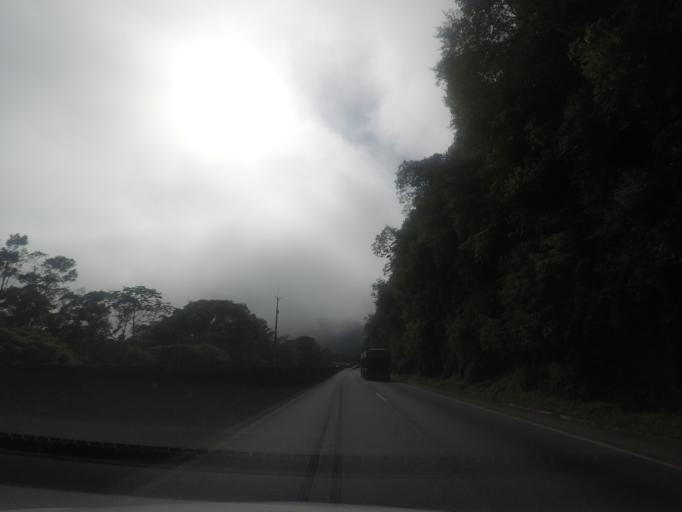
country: BR
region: Parana
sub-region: Antonina
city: Antonina
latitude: -25.5925
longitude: -48.8810
